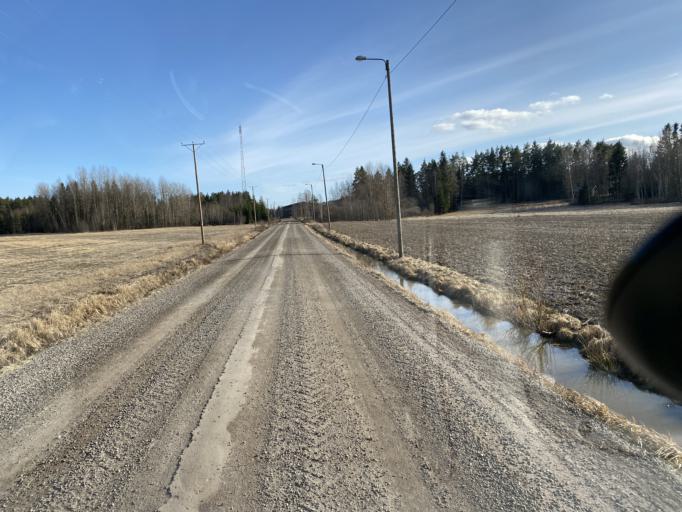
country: FI
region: Satakunta
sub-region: Rauma
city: Lappi
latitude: 61.1317
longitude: 21.9493
